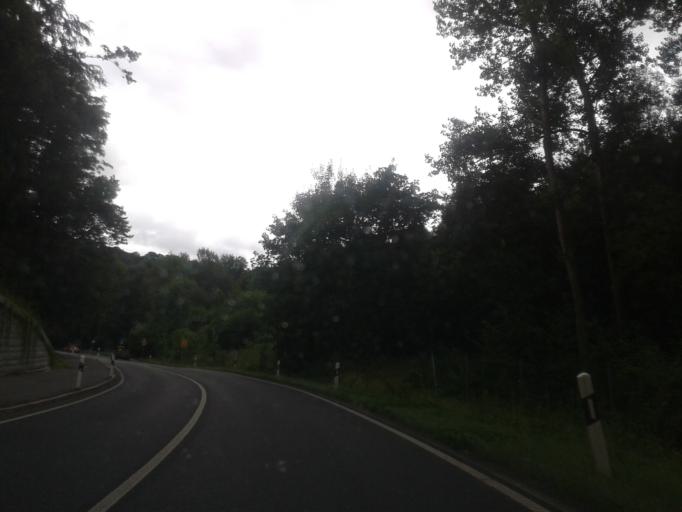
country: DE
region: Saxony
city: Tharandt
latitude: 51.0012
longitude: 13.5690
